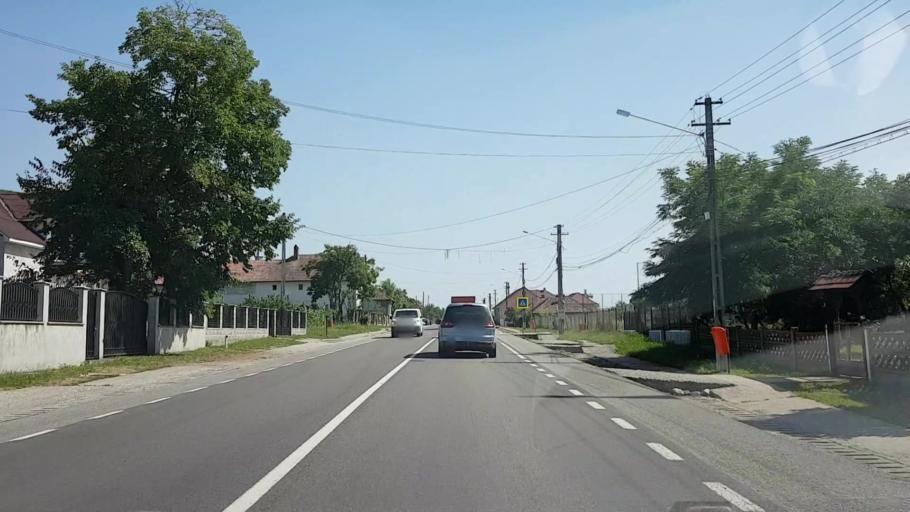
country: RO
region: Bistrita-Nasaud
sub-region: Comuna Sieu-Odorhei
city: Sieu-Odorhei
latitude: 47.1464
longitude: 24.3062
